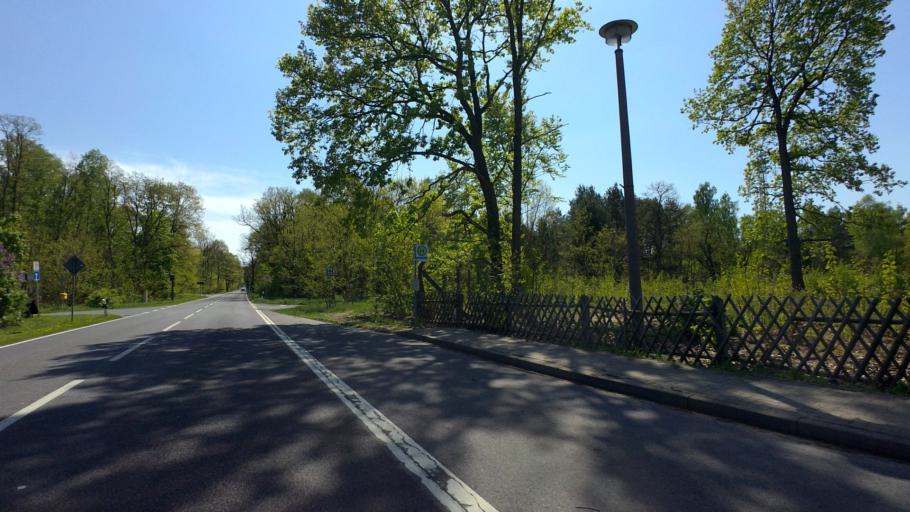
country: DE
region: Brandenburg
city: Gross Koris
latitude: 52.1840
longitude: 13.7068
